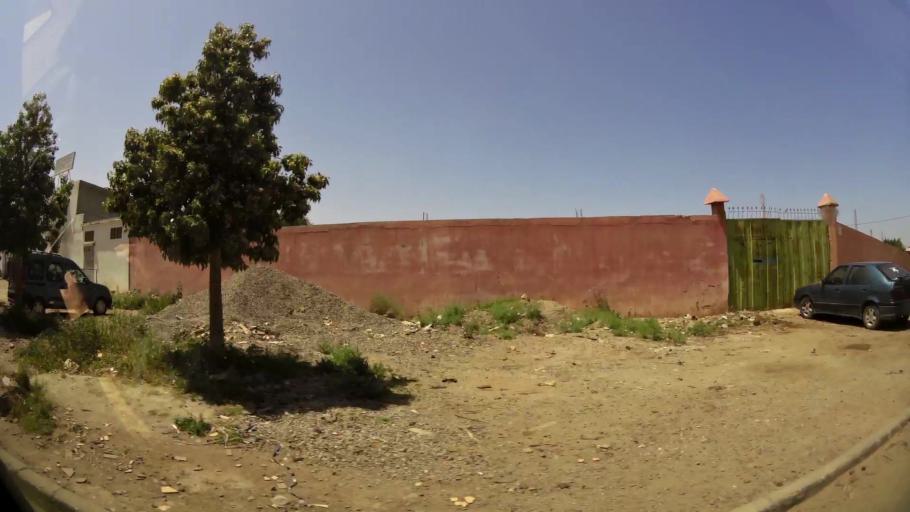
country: MA
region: Souss-Massa-Draa
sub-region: Inezgane-Ait Mellou
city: Inezgane
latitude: 30.3386
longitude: -9.4840
